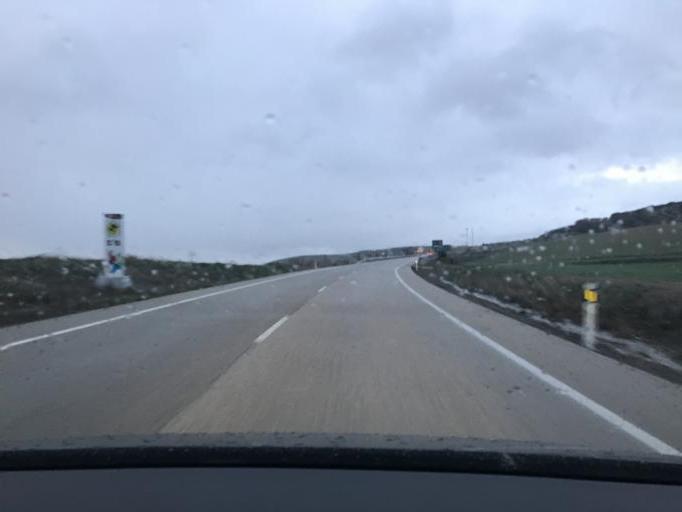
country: ES
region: Andalusia
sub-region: Provincia de Granada
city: Campotejar
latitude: 37.4698
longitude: -3.5779
